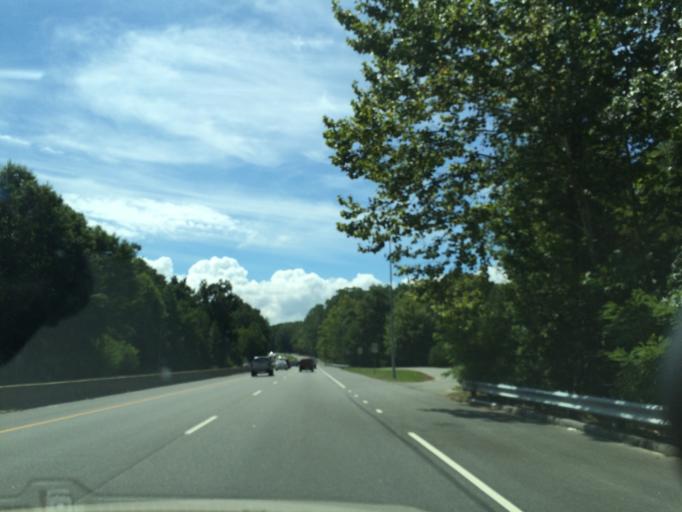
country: US
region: Virginia
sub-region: York County
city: Yorktown
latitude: 37.2347
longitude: -76.5127
